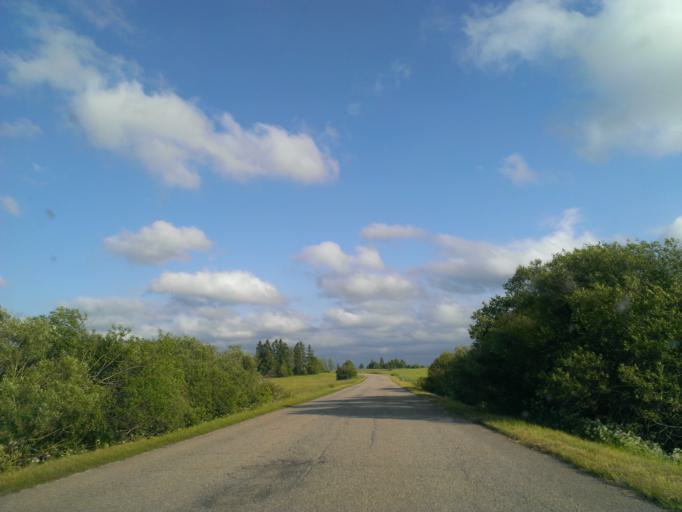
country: LV
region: Aizpute
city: Aizpute
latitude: 56.7624
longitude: 21.5418
